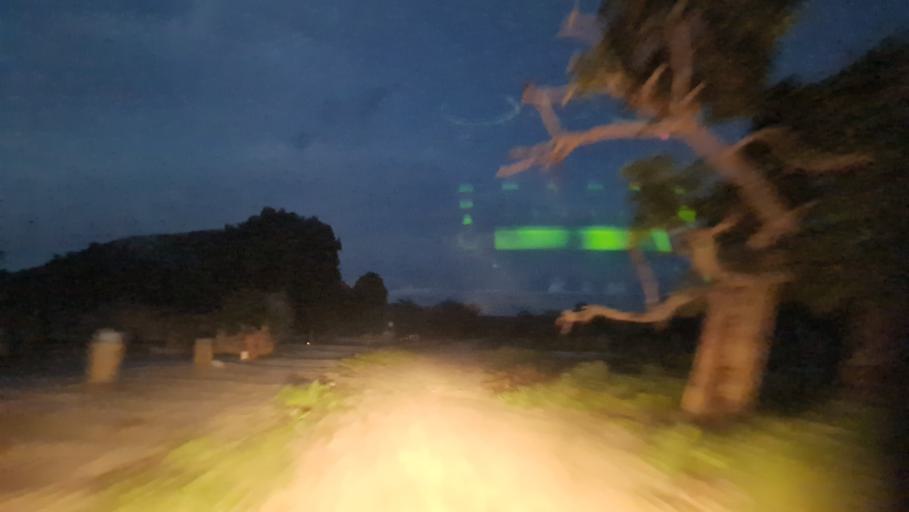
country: MZ
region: Nampula
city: Nampula
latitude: -14.6647
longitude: 39.8370
